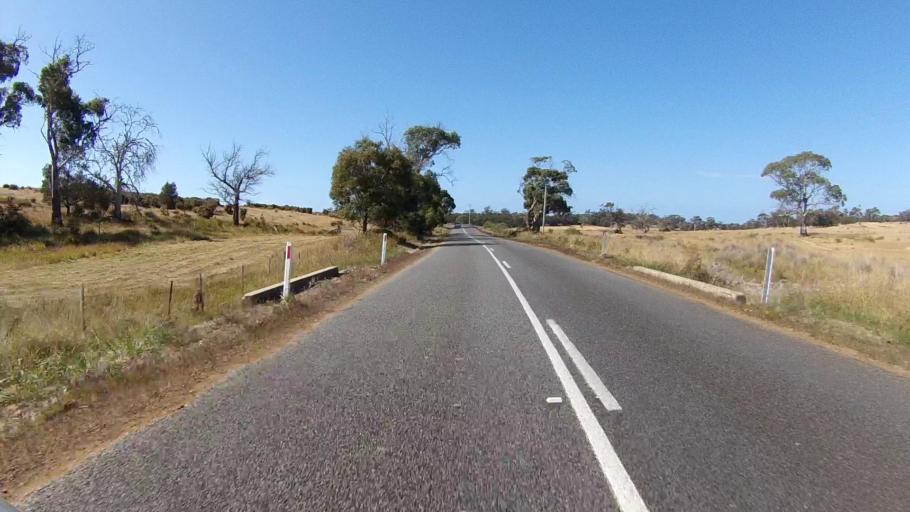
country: AU
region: Tasmania
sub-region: Sorell
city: Sorell
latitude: -42.2970
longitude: 147.9856
